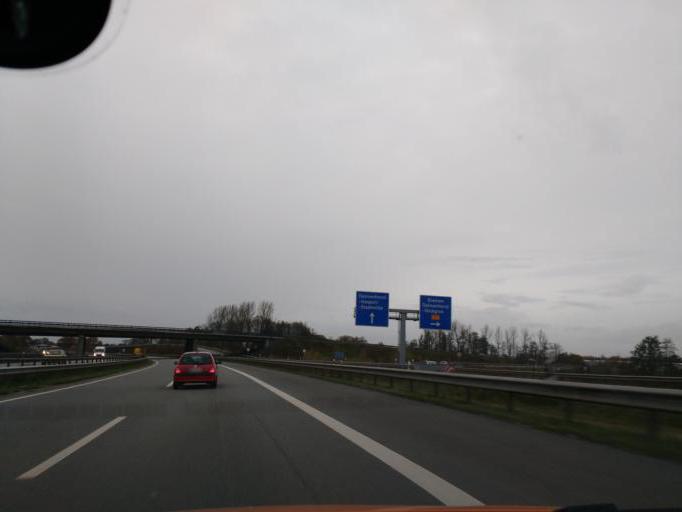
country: DE
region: Lower Saxony
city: Delmenhorst
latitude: 53.0301
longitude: 8.6748
